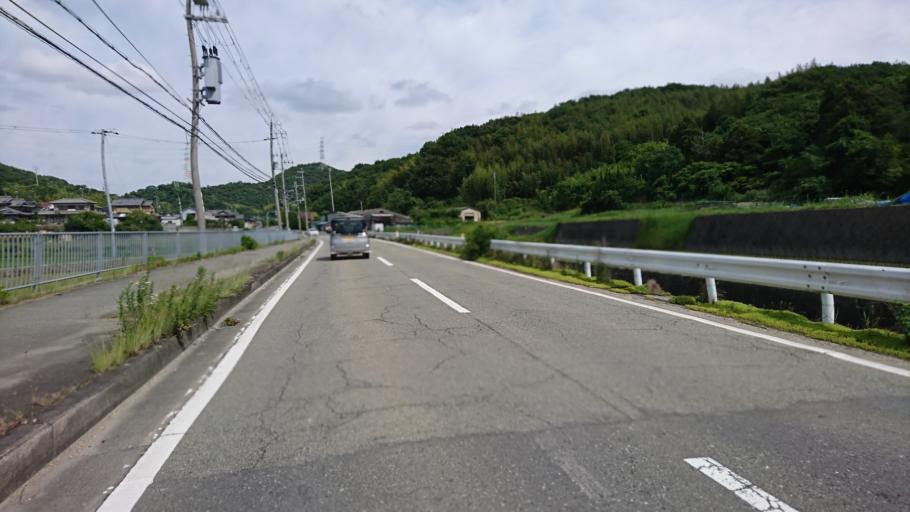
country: JP
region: Hyogo
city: Shirahamacho-usazakiminami
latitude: 34.7956
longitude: 134.7459
